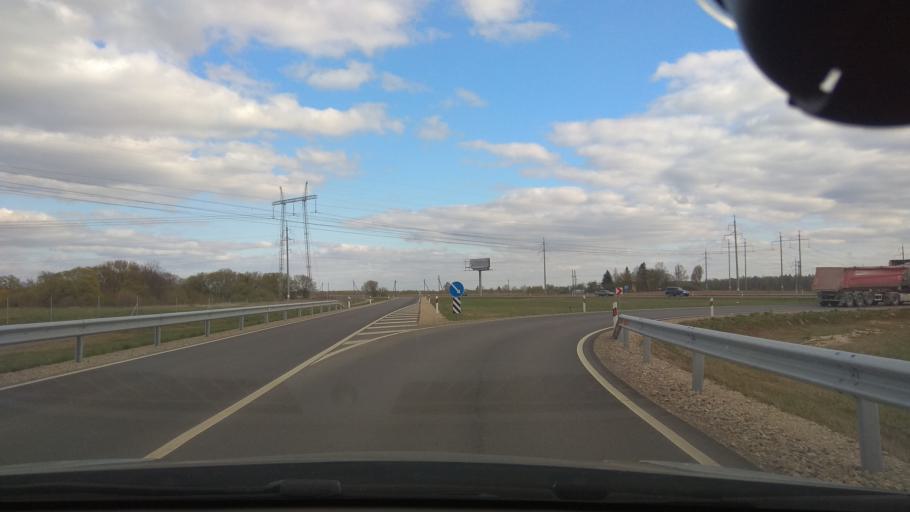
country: LT
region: Panevezys
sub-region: Panevezys City
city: Panevezys
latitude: 55.7343
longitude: 24.2793
